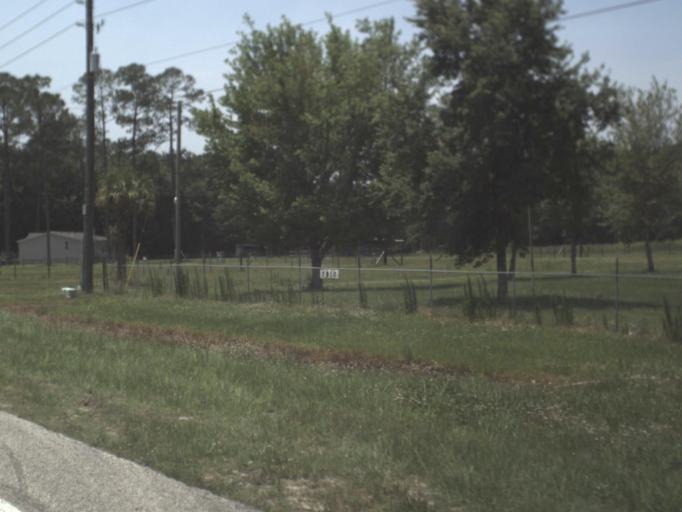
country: US
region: Florida
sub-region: Duval County
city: Baldwin
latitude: 30.2104
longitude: -82.0114
